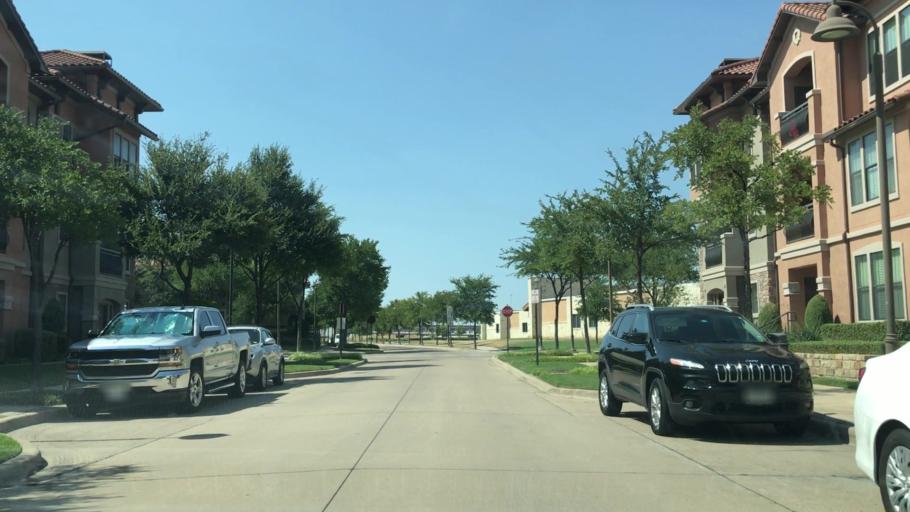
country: US
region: Texas
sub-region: Dallas County
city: Farmers Branch
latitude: 32.9013
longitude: -96.9372
